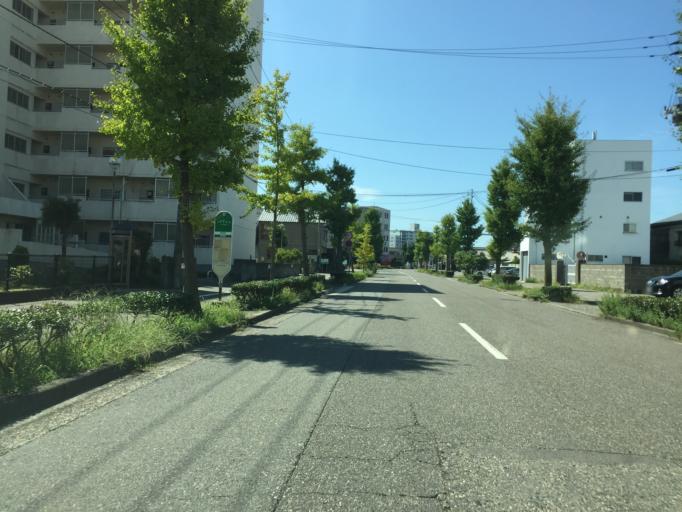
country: JP
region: Niigata
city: Niigata-shi
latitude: 37.9329
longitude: 139.0541
